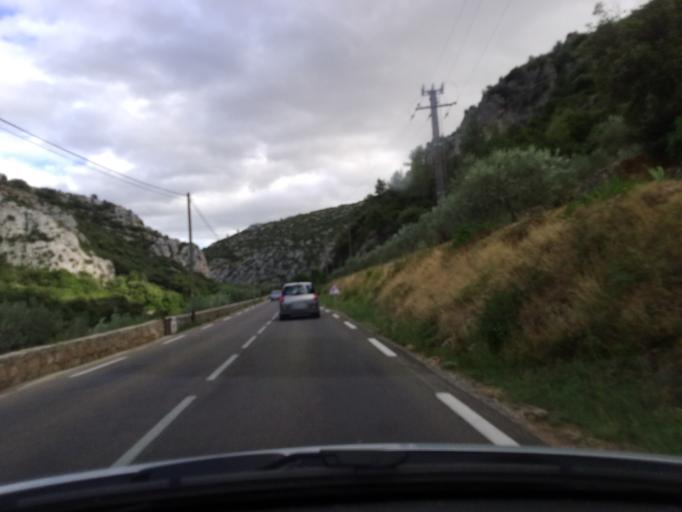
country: FR
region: Languedoc-Roussillon
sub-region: Departement de l'Herault
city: Saint-Jean-de-Fos
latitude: 43.7148
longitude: 3.5524
